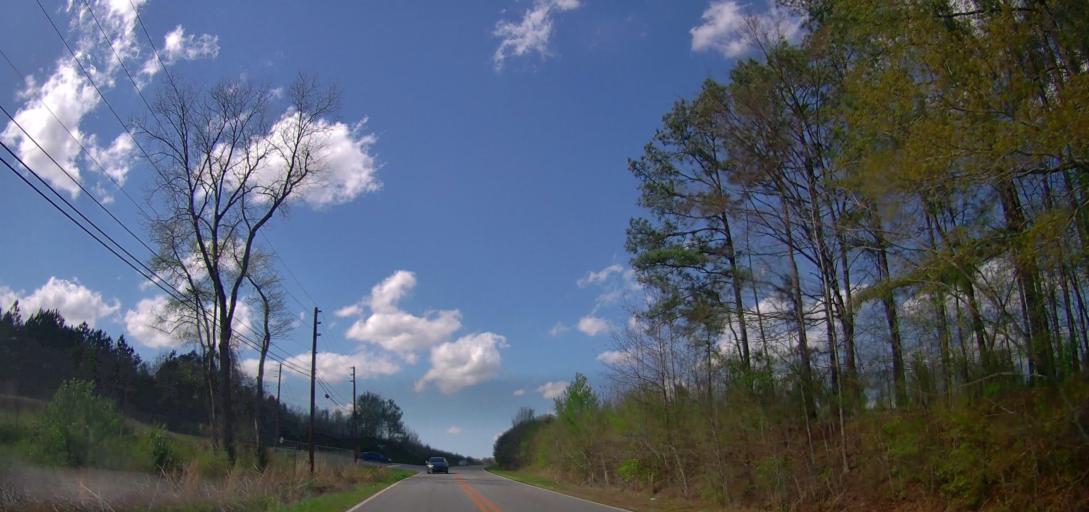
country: US
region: Georgia
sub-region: Bibb County
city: Macon
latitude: 32.8201
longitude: -83.5537
